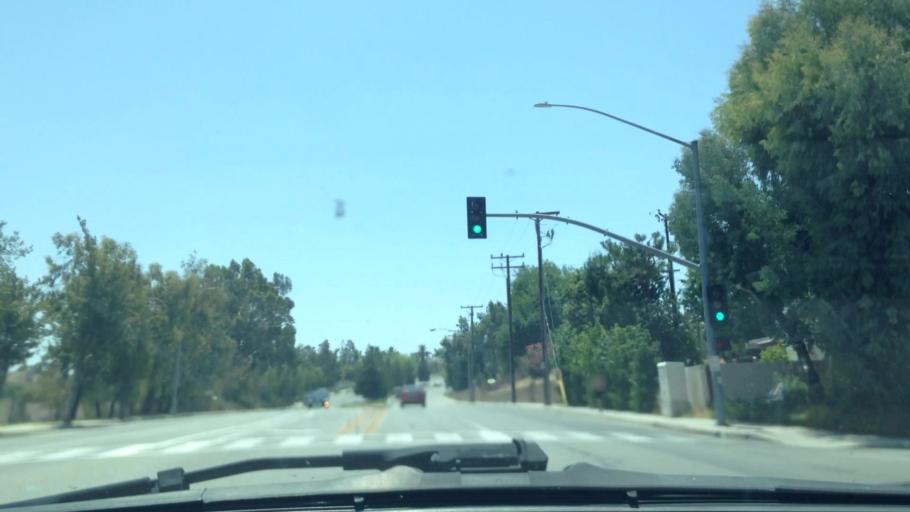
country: US
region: California
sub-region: Orange County
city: Brea
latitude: 33.9035
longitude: -117.8899
